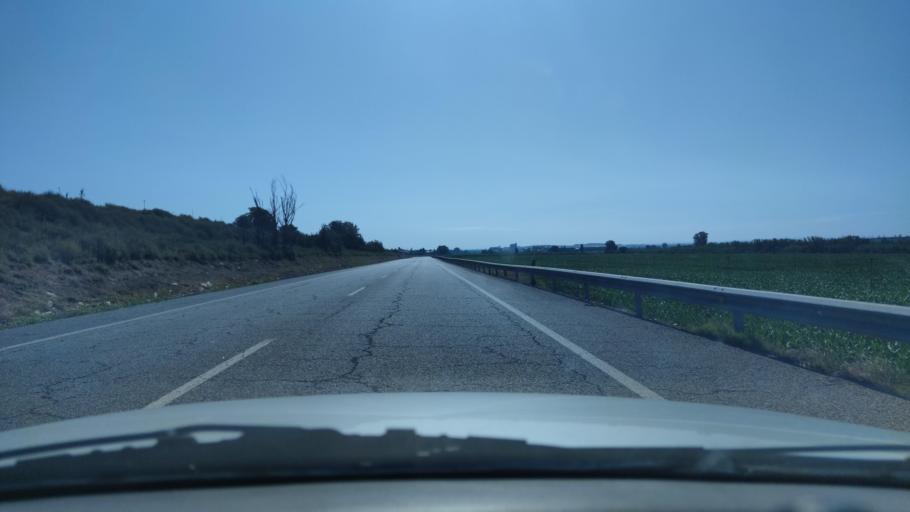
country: ES
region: Catalonia
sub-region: Provincia de Lleida
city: Bellvis
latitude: 41.6285
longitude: 0.7622
